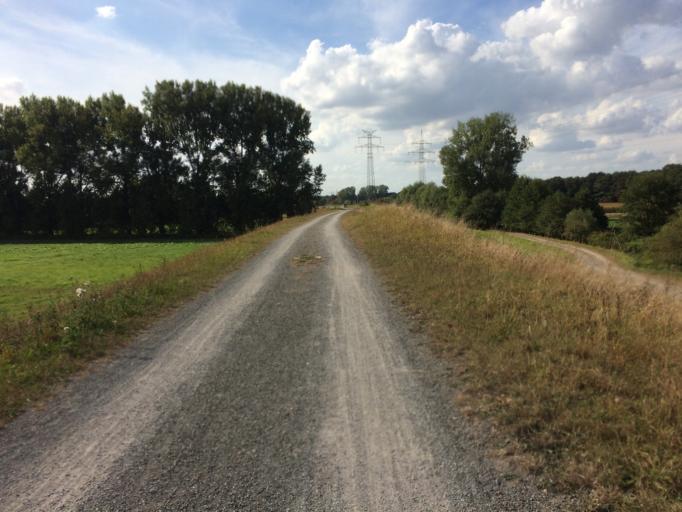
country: DE
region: North Rhine-Westphalia
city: Marl
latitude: 51.6998
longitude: 7.0884
